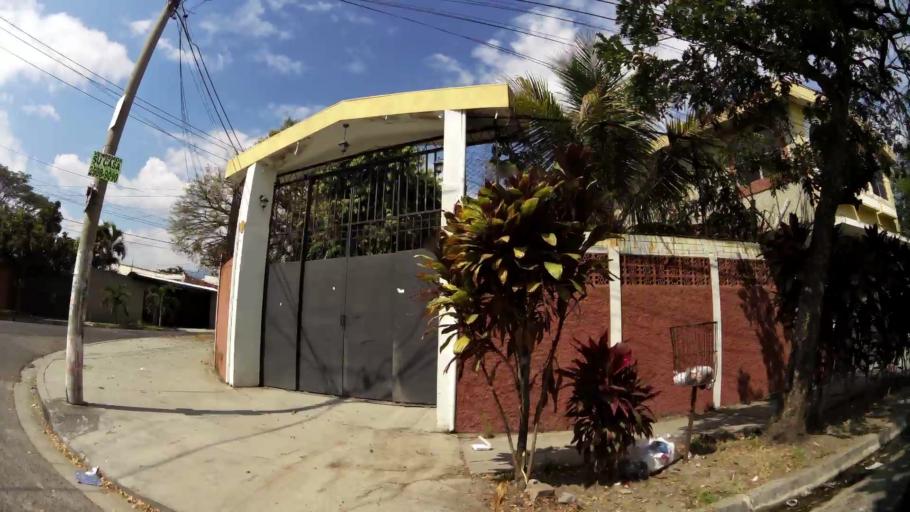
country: SV
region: San Salvador
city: Mejicanos
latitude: 13.7073
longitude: -89.2168
